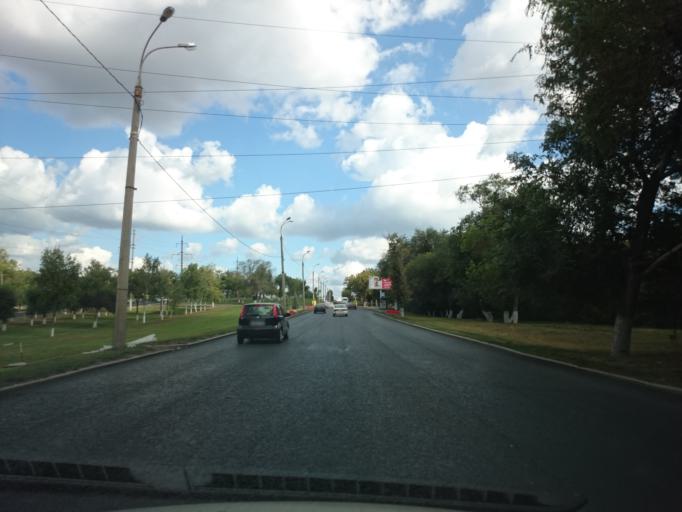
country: RU
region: Samara
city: Samara
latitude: 53.2258
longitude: 50.1732
